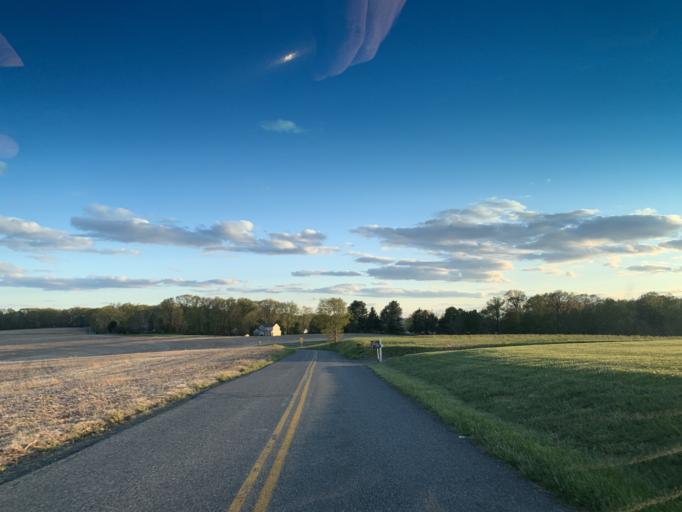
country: US
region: Maryland
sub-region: Harford County
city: Jarrettsville
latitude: 39.6599
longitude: -76.4134
